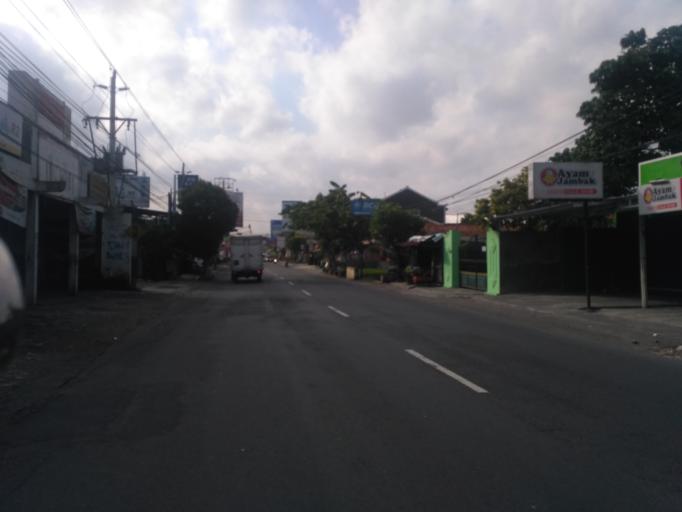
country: ID
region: Daerah Istimewa Yogyakarta
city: Yogyakarta
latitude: -7.7789
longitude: 110.3399
